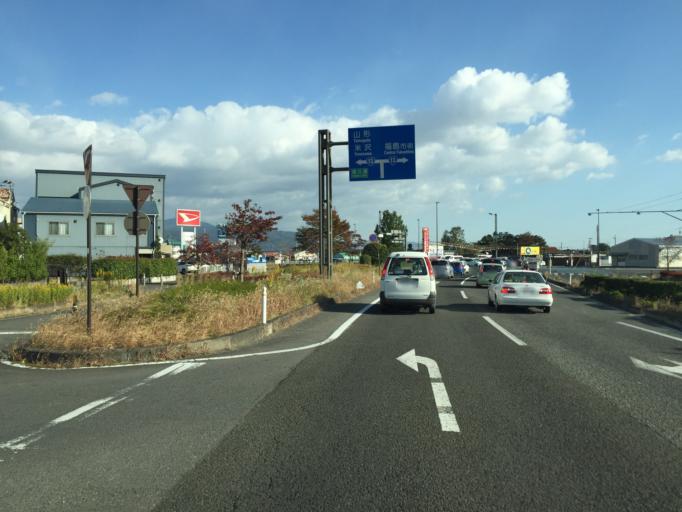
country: JP
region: Fukushima
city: Fukushima-shi
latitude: 37.7896
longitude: 140.4604
